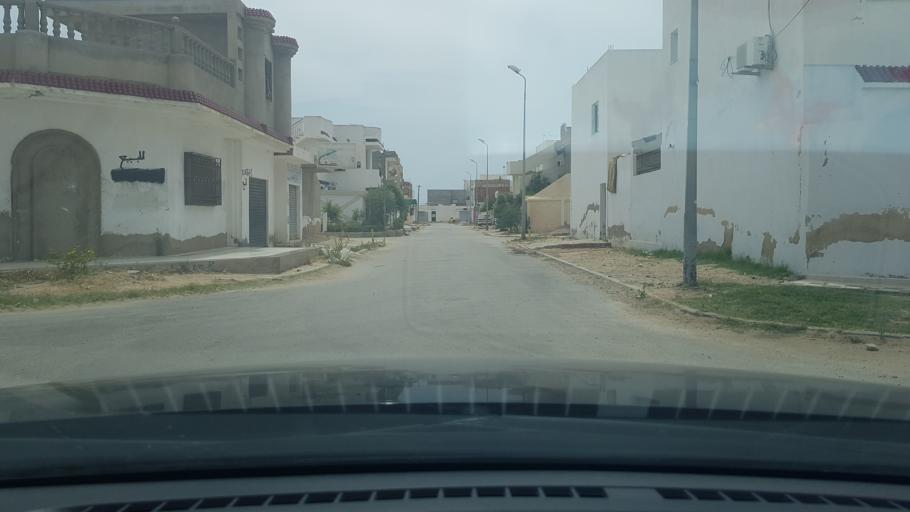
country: TN
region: Safaqis
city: Al Qarmadah
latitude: 34.8259
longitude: 10.7469
